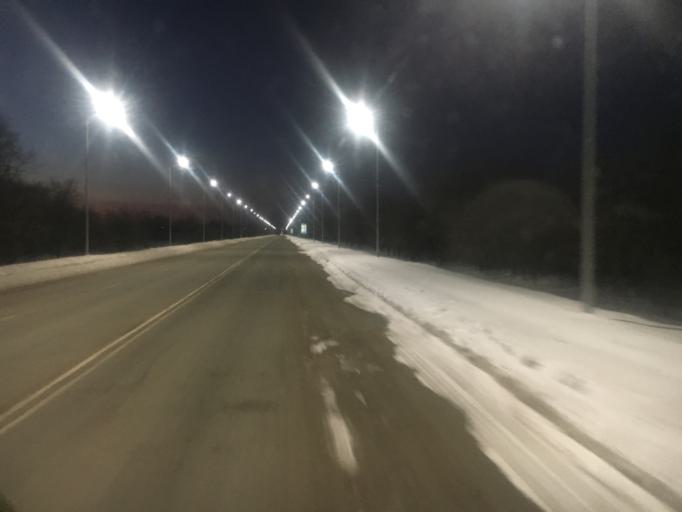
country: KZ
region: Batys Qazaqstan
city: Oral
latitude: 51.1580
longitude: 51.5332
